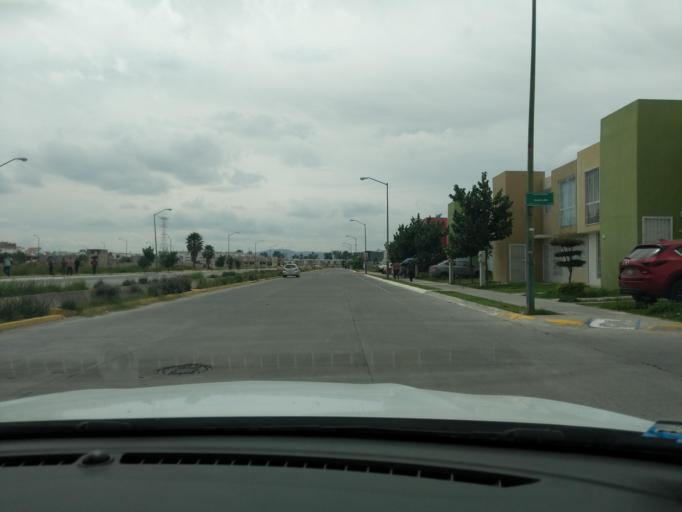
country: MX
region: Jalisco
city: Tesistan
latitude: 20.7898
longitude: -103.4890
